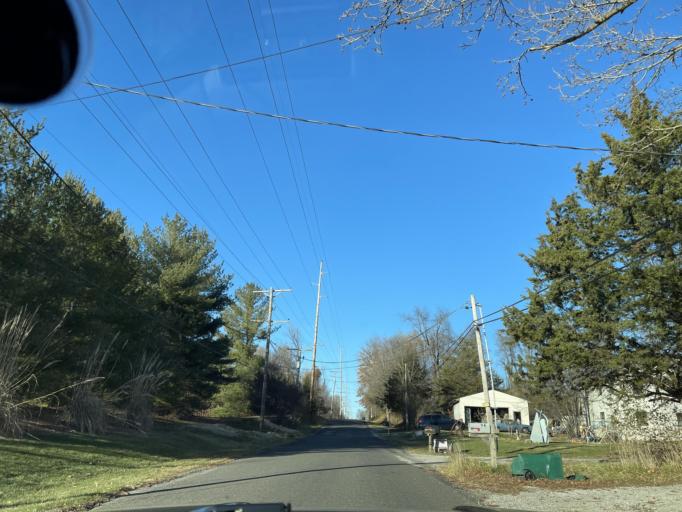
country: US
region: Illinois
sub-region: Sangamon County
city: Leland Grove
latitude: 39.8026
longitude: -89.7154
